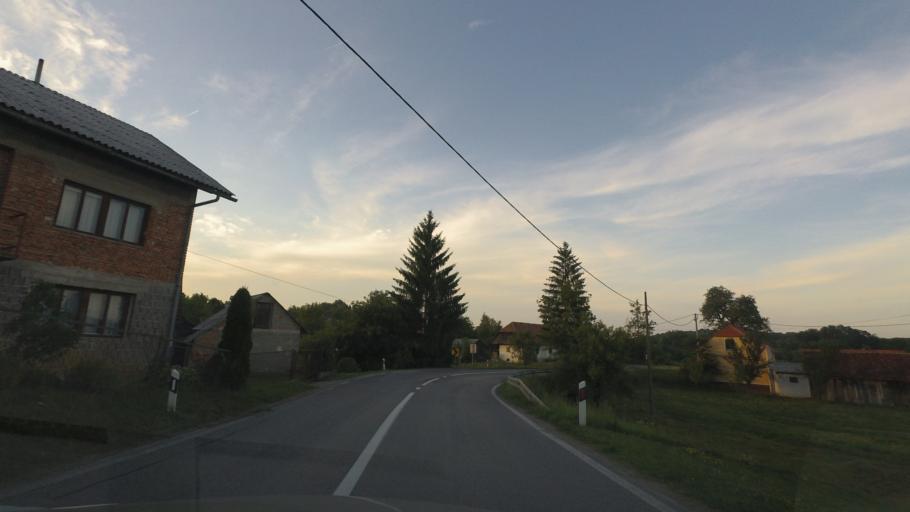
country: HR
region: Karlovacka
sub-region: Grad Karlovac
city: Karlovac
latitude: 45.4078
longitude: 15.4489
